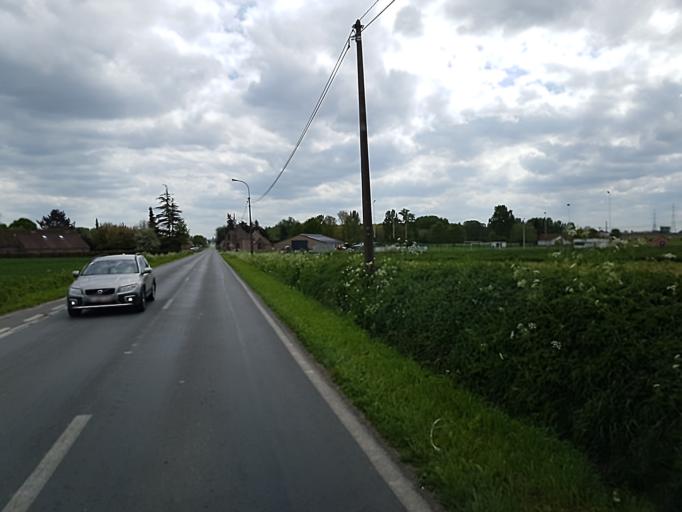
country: BE
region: Wallonia
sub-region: Province du Hainaut
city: Celles
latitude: 50.7401
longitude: 3.4510
